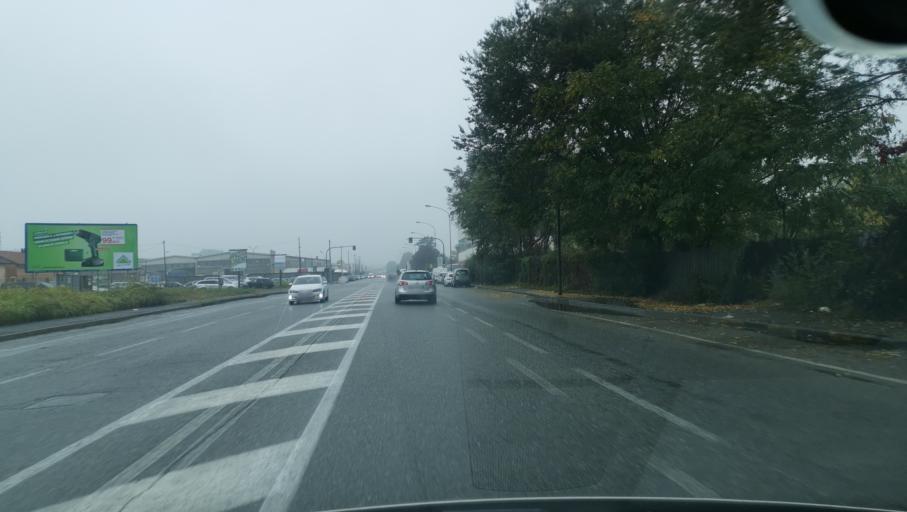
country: IT
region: Piedmont
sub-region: Provincia di Torino
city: Turin
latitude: 45.1101
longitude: 7.6795
